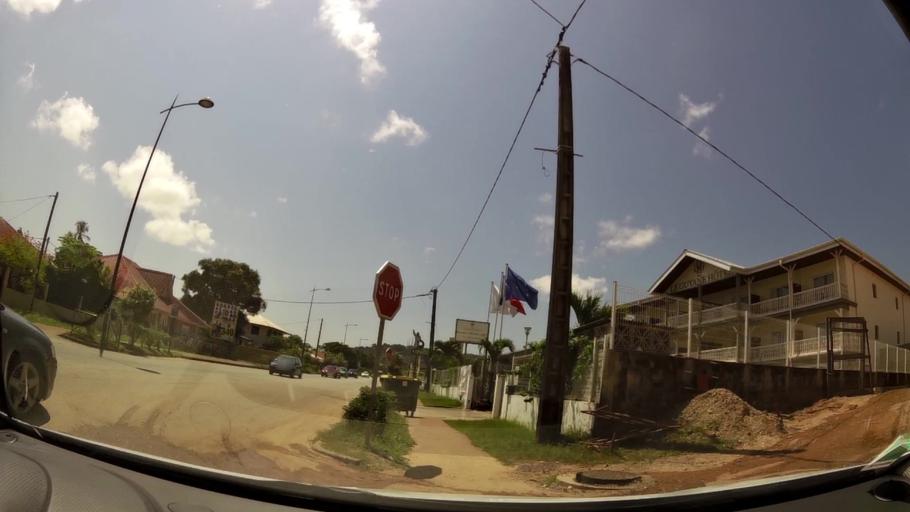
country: GF
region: Guyane
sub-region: Guyane
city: Cayenne
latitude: 4.9203
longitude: -52.3205
